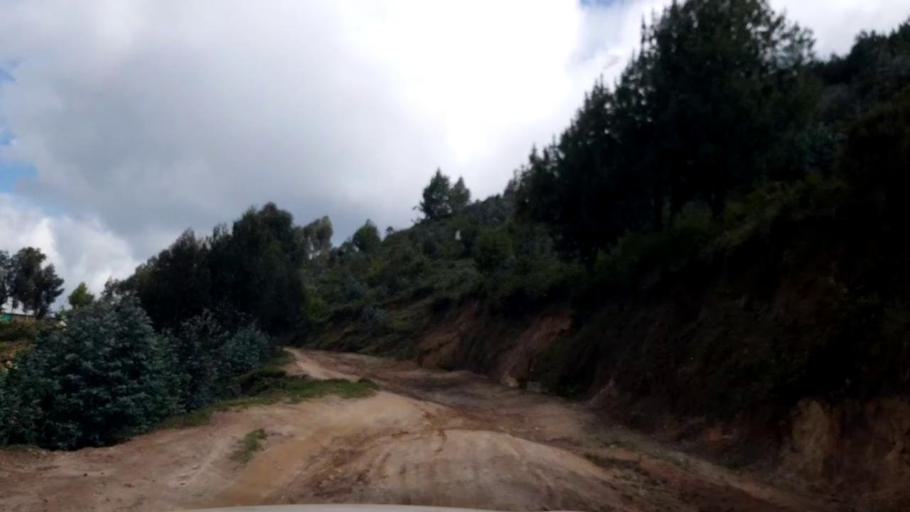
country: RW
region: Western Province
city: Kibuye
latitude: -1.8806
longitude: 29.4770
